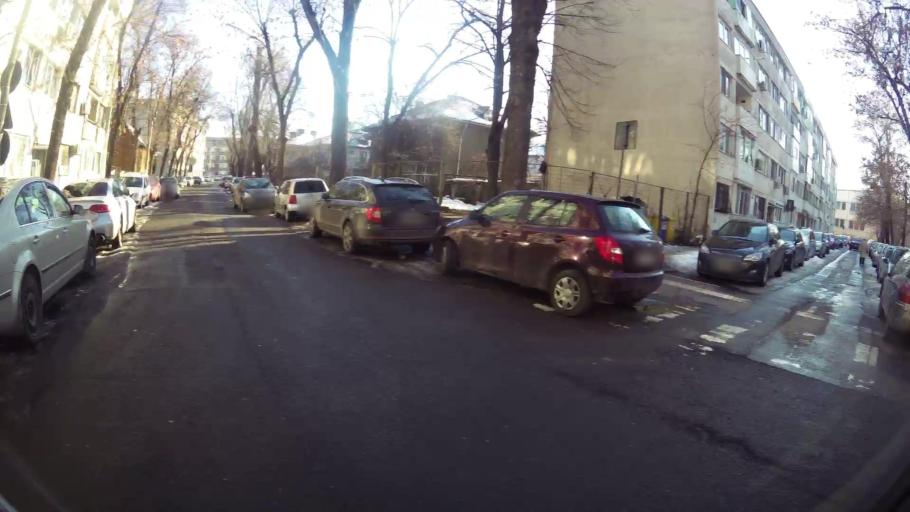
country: RO
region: Bucuresti
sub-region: Municipiul Bucuresti
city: Bucuresti
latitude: 44.4051
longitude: 26.0948
